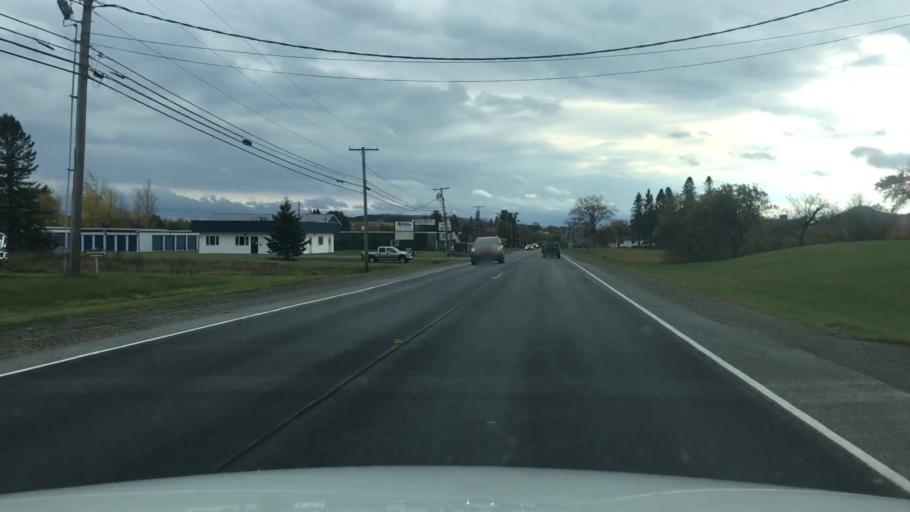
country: US
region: Maine
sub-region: Aroostook County
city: Presque Isle
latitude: 46.6580
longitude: -68.0069
